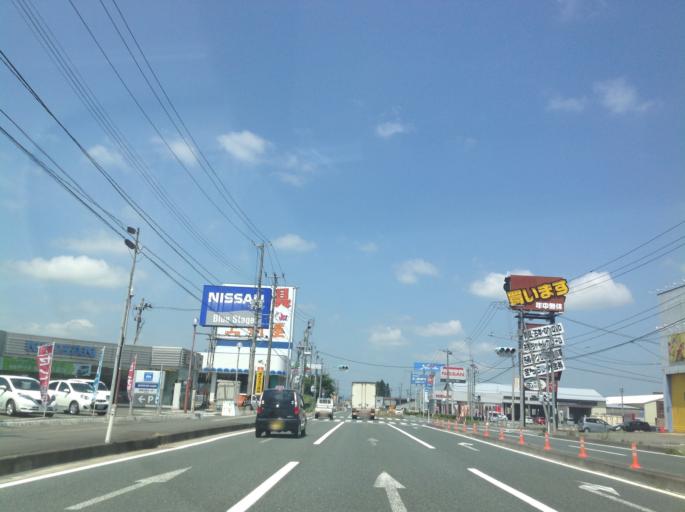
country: JP
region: Iwate
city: Kitakami
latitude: 39.3164
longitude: 141.1124
